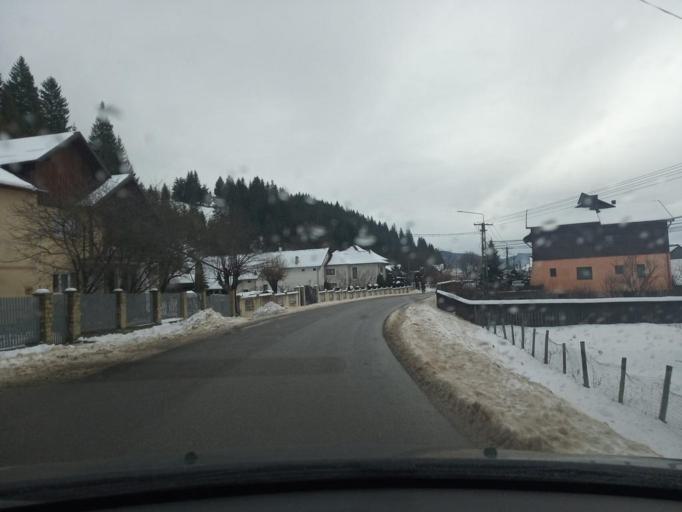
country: RO
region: Suceava
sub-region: Comuna Manastirea Humorului
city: Manastirea Humorului
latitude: 47.5897
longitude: 25.8678
